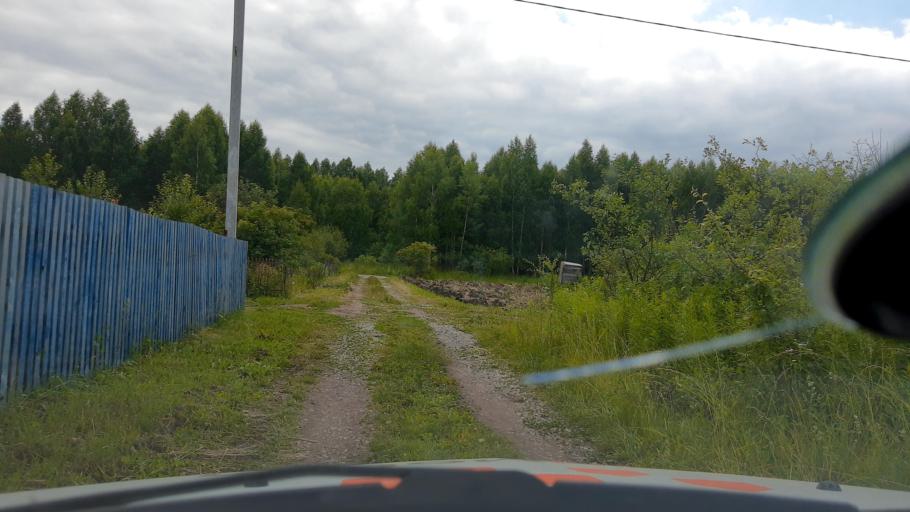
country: RU
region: Bashkortostan
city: Kabakovo
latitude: 54.7170
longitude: 56.2020
